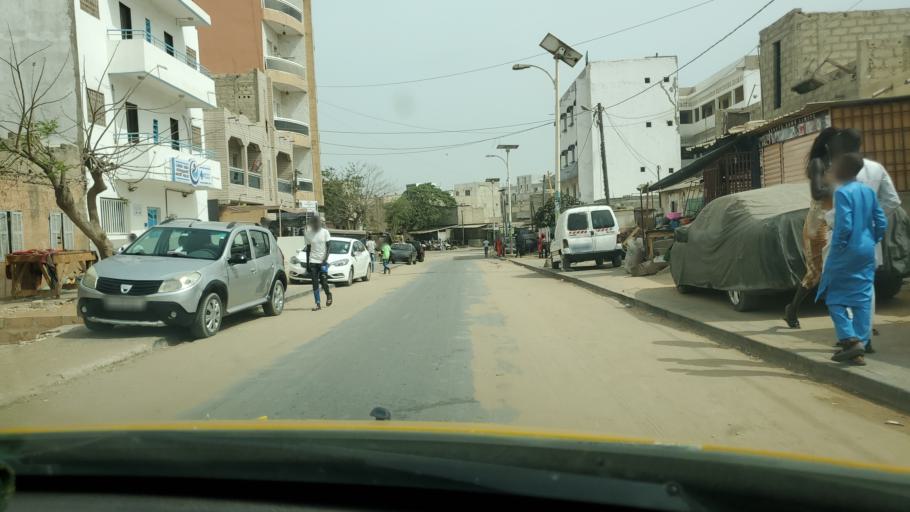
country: SN
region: Dakar
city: Pikine
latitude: 14.7708
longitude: -17.3941
